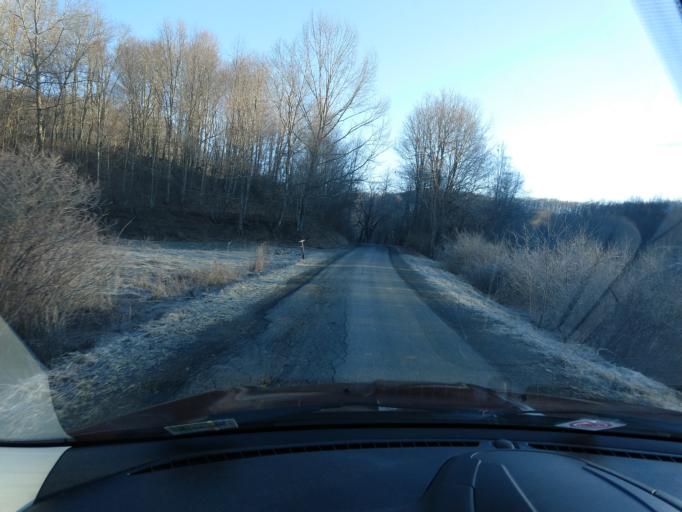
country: US
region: West Virginia
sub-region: Greenbrier County
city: Rainelle
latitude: 37.9017
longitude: -80.7327
